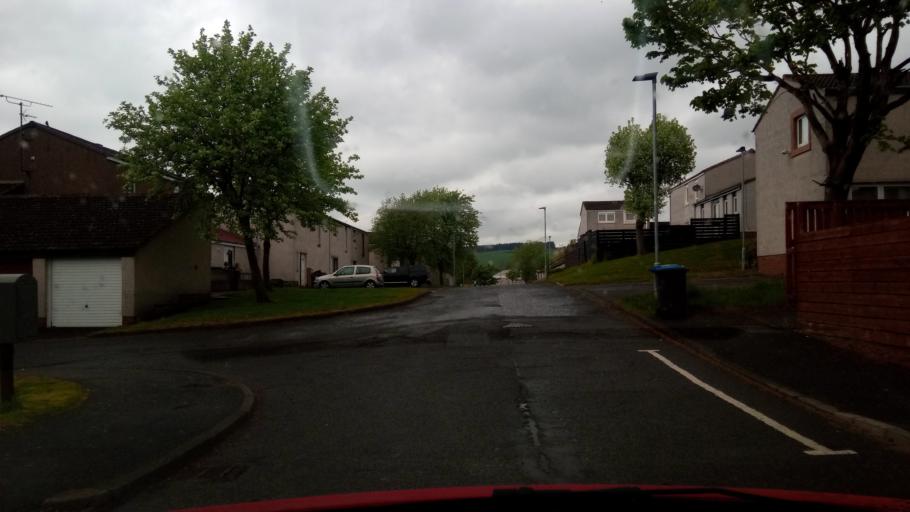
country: GB
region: Scotland
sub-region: The Scottish Borders
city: Jedburgh
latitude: 55.4739
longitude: -2.5438
